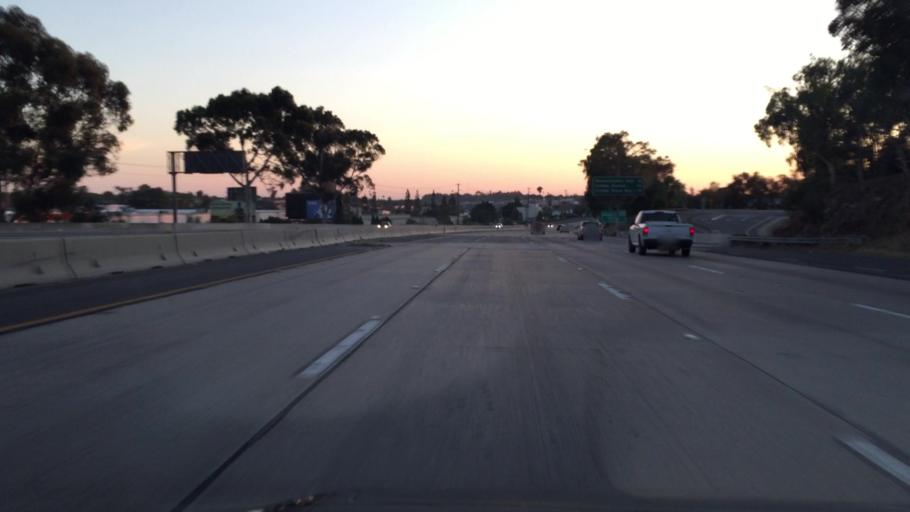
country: US
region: California
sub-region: San Diego County
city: Lemon Grove
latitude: 32.7457
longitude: -117.0339
